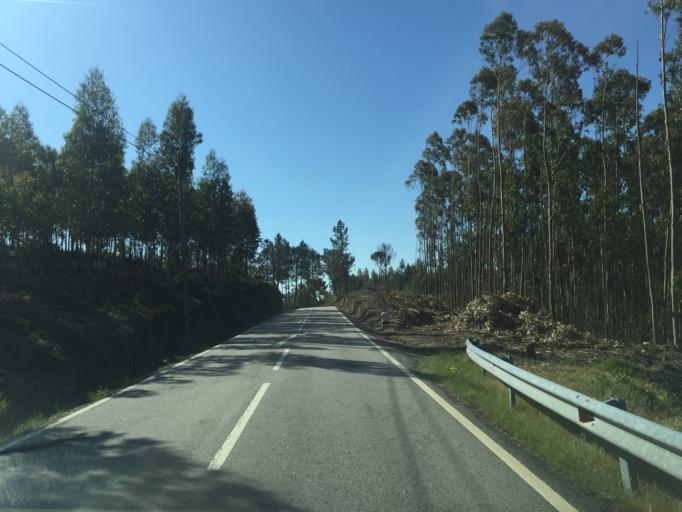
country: PT
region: Coimbra
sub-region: Pampilhosa da Serra
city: Pampilhosa da Serra
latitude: 40.0424
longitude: -7.8803
